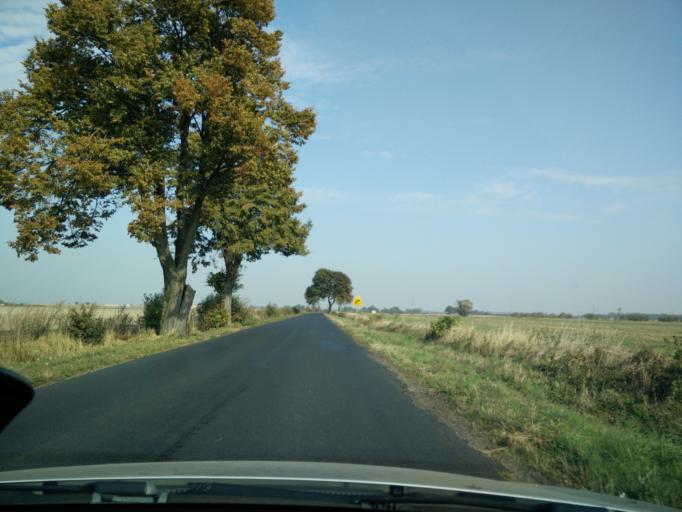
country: PL
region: Greater Poland Voivodeship
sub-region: Powiat sredzki
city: Dominowo
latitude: 52.2799
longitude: 17.3210
